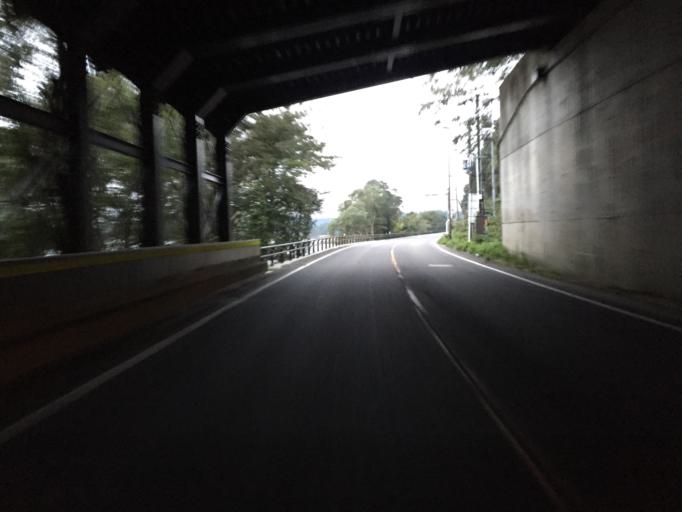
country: JP
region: Fukushima
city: Inawashiro
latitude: 37.5123
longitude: 140.0289
